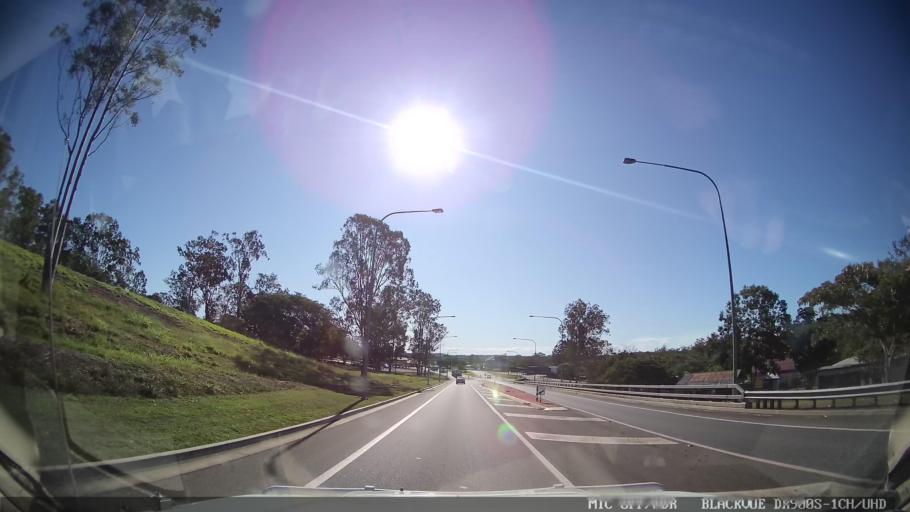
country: AU
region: Queensland
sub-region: Bundaberg
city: Sharon
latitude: -24.9947
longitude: 151.9596
